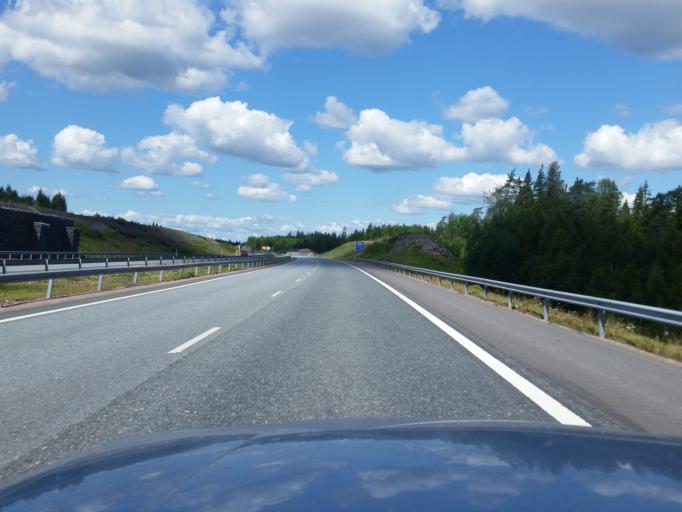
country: FI
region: Uusimaa
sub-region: Helsinki
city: Sammatti
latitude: 60.3634
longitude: 23.8814
